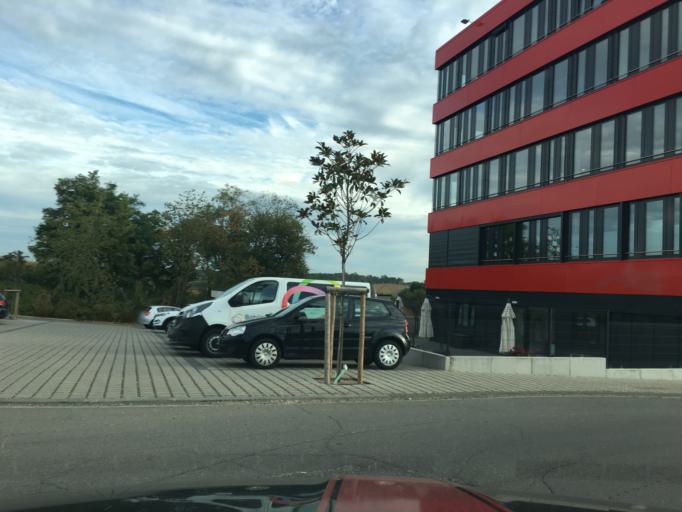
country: LU
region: Luxembourg
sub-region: Canton d'Esch-sur-Alzette
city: Bettembourg
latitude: 49.5318
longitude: 6.1095
